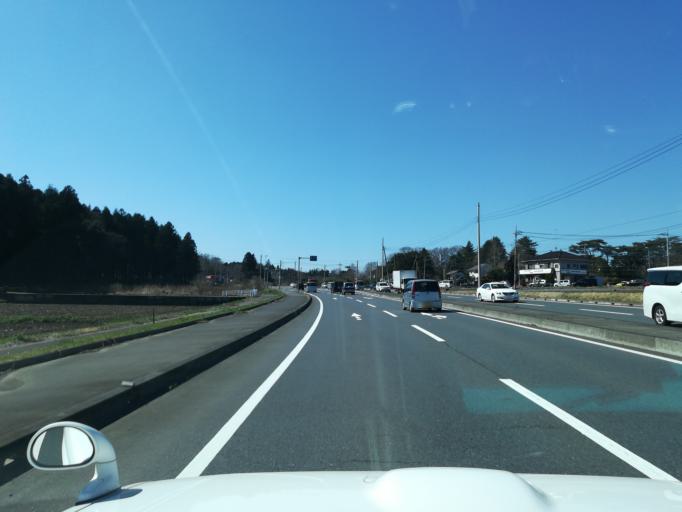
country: JP
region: Ibaraki
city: Ushiku
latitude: 35.9688
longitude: 140.1729
